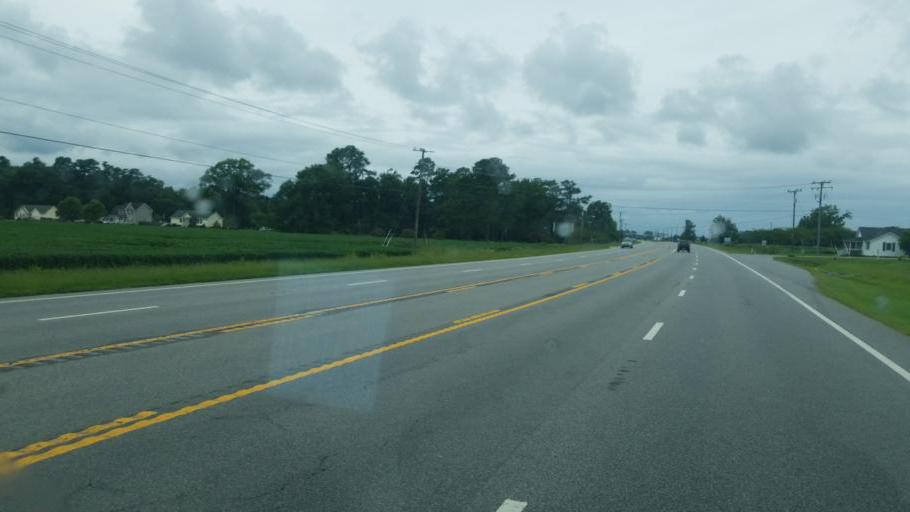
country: US
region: North Carolina
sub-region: Currituck County
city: Currituck
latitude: 36.3899
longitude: -75.9787
